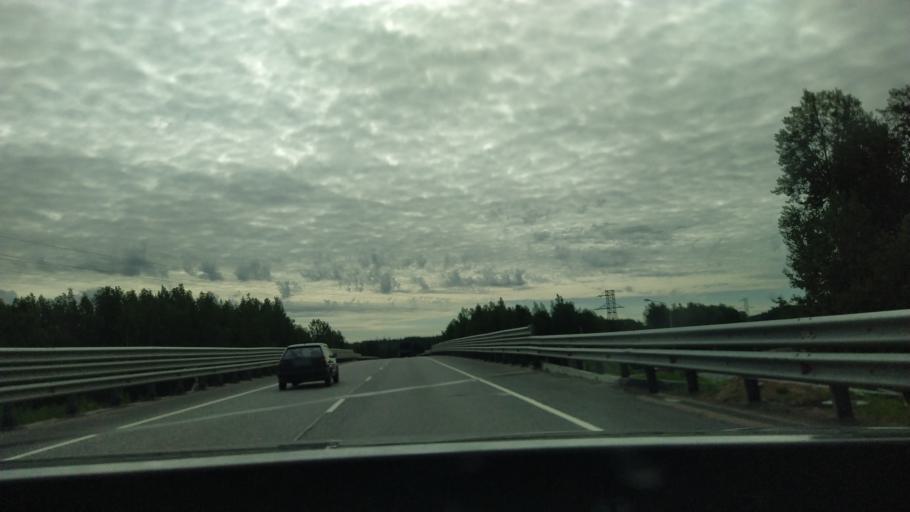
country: RU
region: Leningrad
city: Ul'yanovka
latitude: 59.5933
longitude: 30.7773
